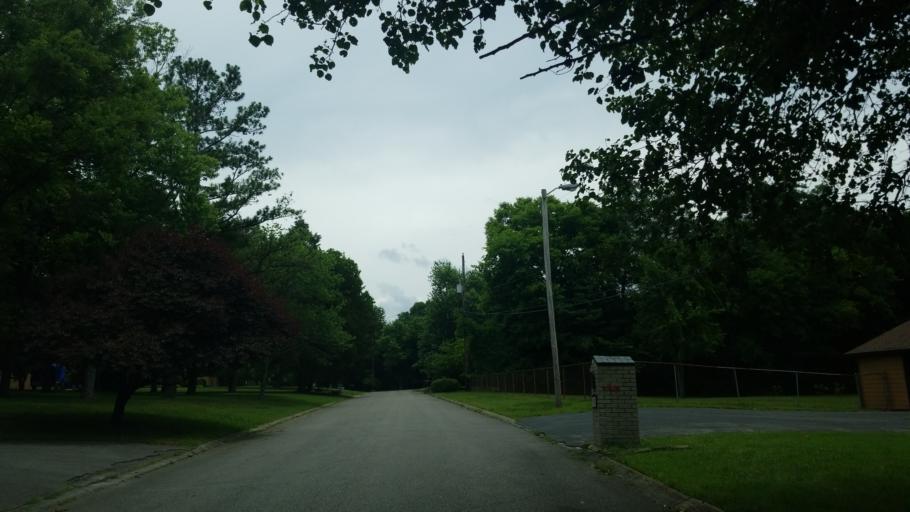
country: US
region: Tennessee
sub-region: Williamson County
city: Brentwood Estates
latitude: 36.0271
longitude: -86.7836
